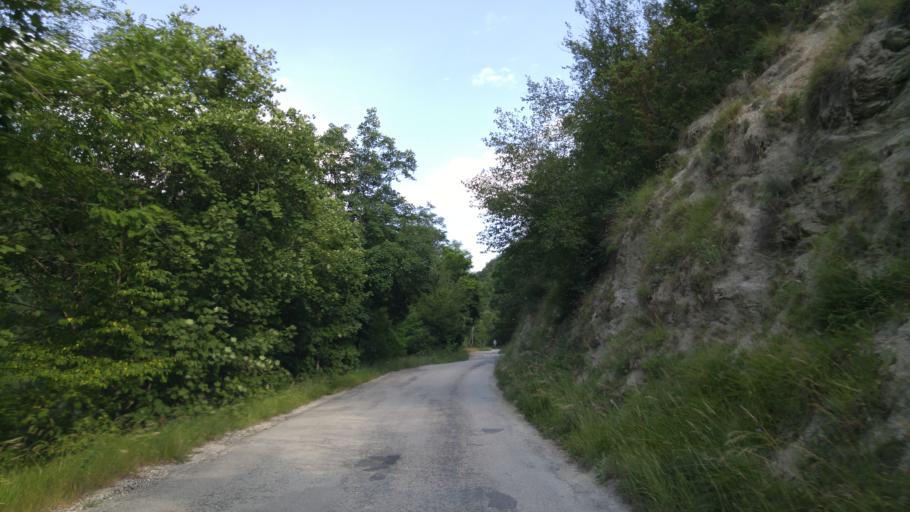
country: IT
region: The Marches
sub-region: Provincia di Pesaro e Urbino
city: Acqualagna
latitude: 43.6312
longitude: 12.7163
